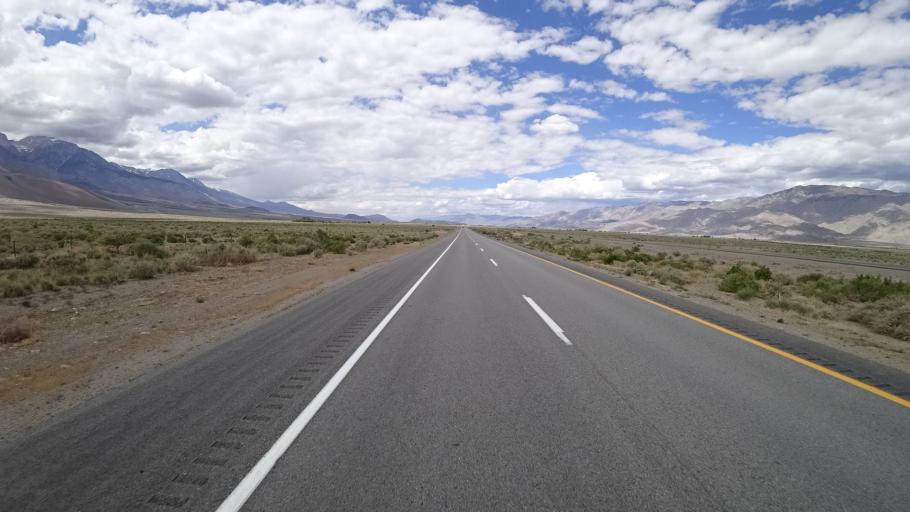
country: US
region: California
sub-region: Inyo County
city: Big Pine
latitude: 36.8960
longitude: -118.2424
